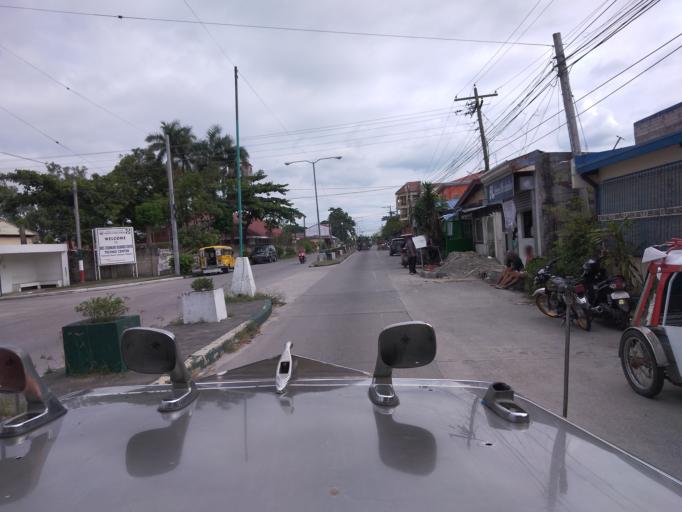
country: PH
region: Central Luzon
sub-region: Province of Pampanga
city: Pandacaqui
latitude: 15.1801
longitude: 120.6431
